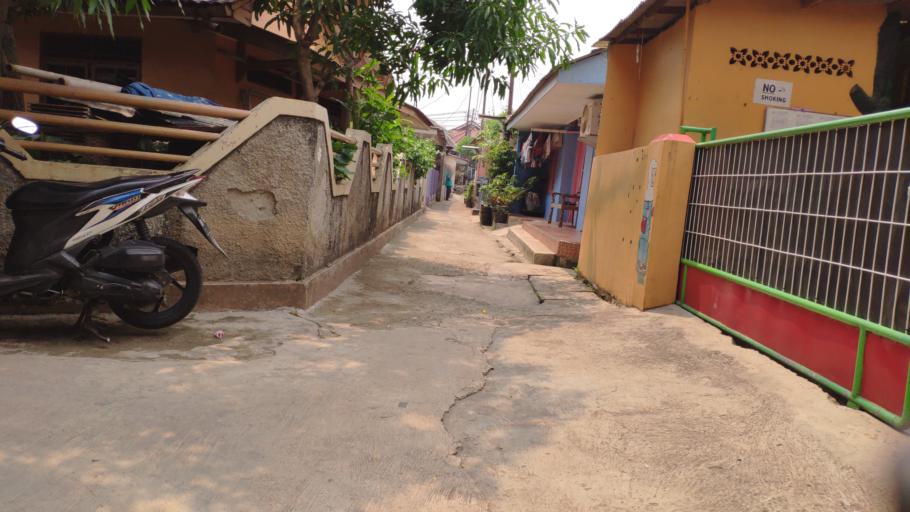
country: ID
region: West Java
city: Depok
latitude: -6.3697
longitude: 106.8074
